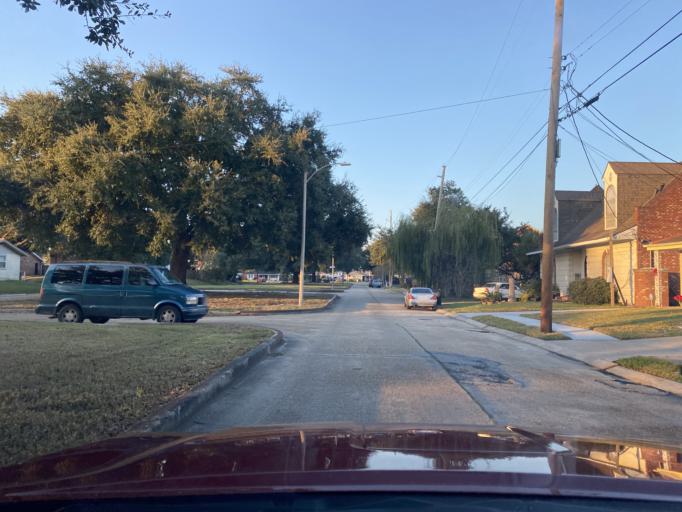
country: US
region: Louisiana
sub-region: Orleans Parish
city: New Orleans
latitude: 30.0240
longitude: -90.0564
